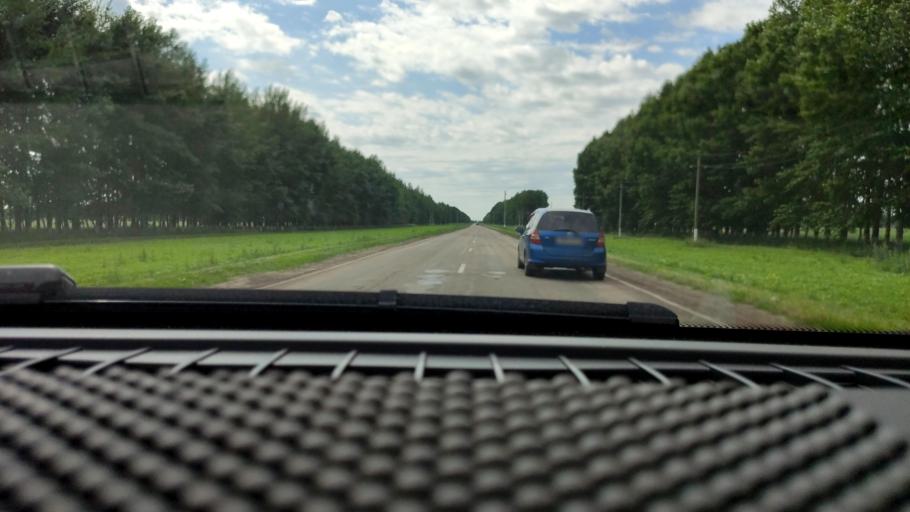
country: RU
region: Voronezj
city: Panino
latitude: 51.6515
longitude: 40.0933
